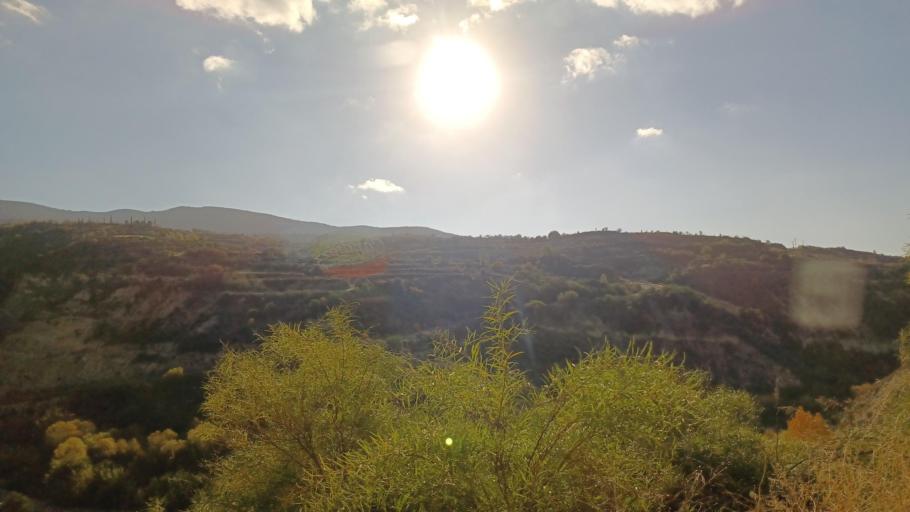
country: CY
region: Limassol
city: Pachna
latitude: 34.8580
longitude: 32.7267
